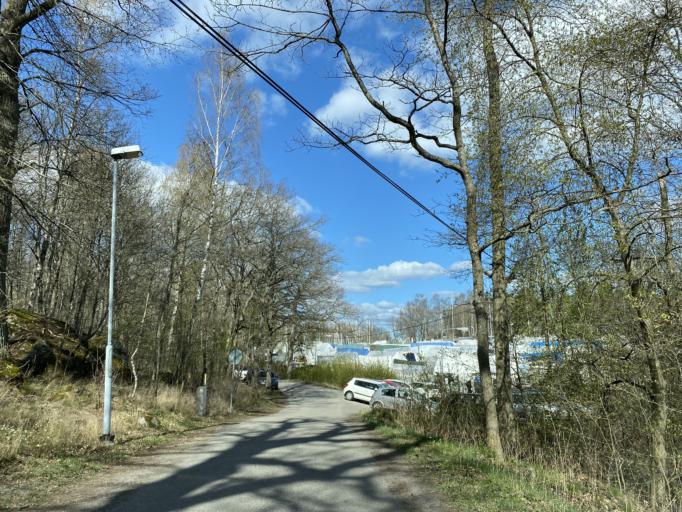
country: SE
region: Stockholm
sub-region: Nacka Kommun
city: Nacka
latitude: 59.3276
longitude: 18.1494
